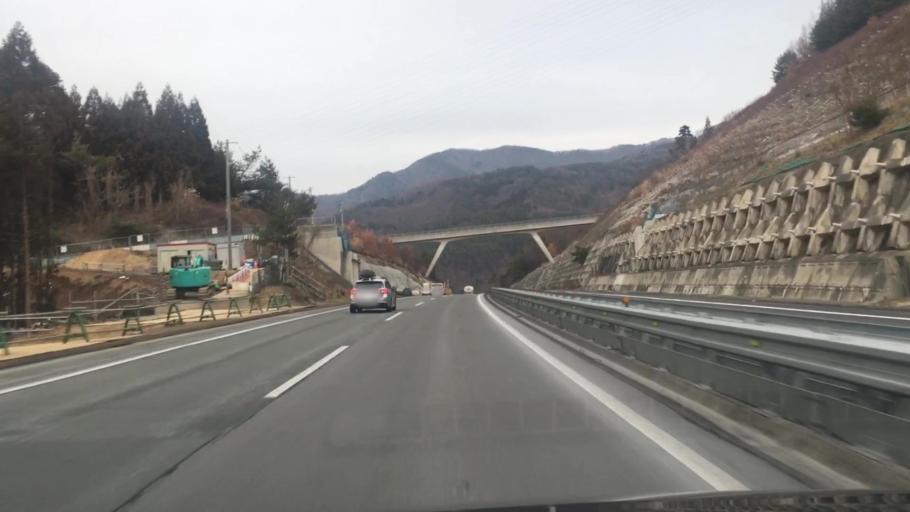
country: JP
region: Nagano
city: Ueda
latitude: 36.4644
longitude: 138.1980
